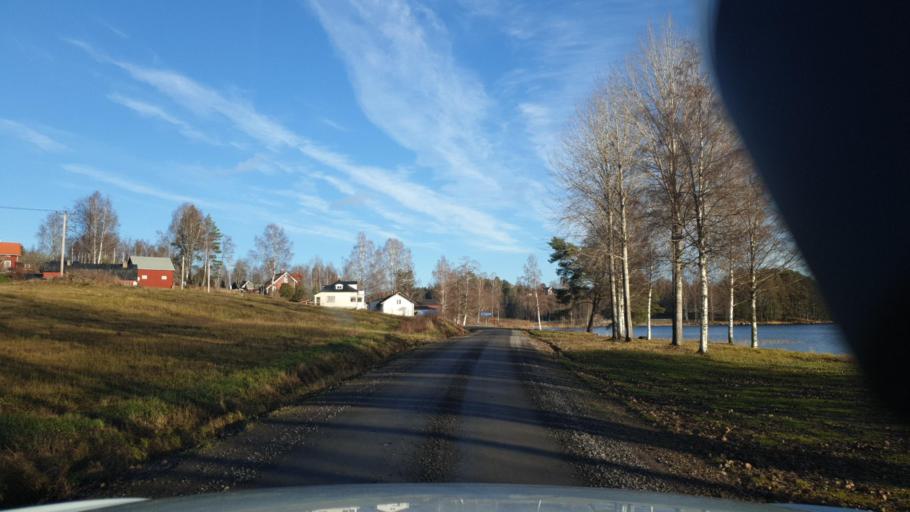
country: NO
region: Ostfold
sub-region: Romskog
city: Romskog
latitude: 59.8527
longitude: 11.9651
